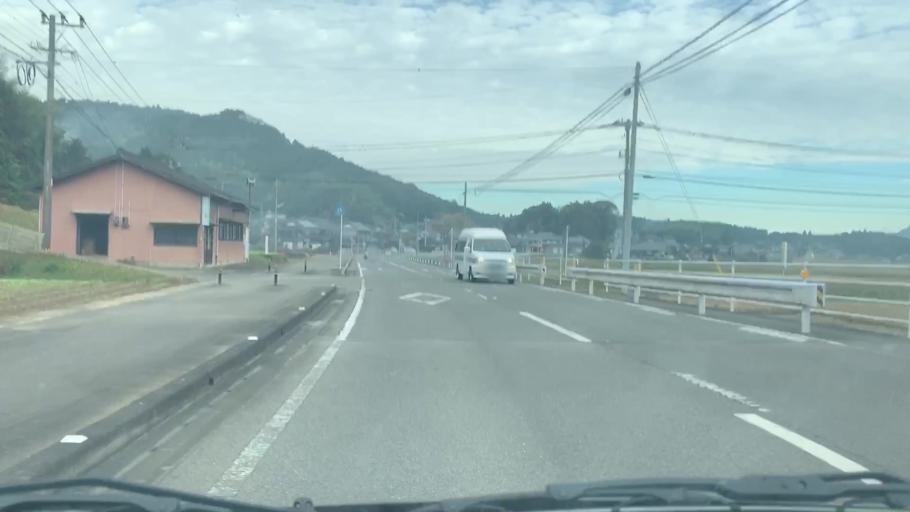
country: JP
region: Saga Prefecture
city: Takeocho-takeo
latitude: 33.1983
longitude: 129.9615
